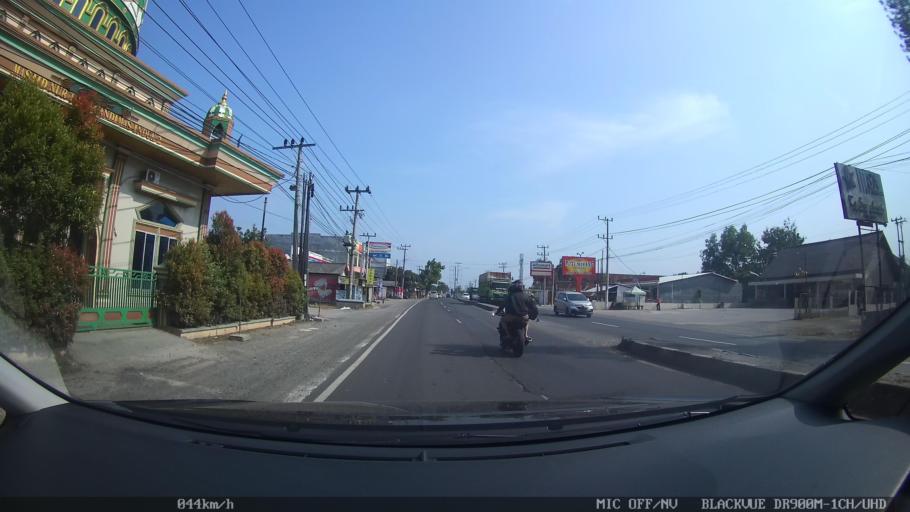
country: ID
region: Lampung
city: Natar
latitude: -5.2709
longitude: 105.1866
